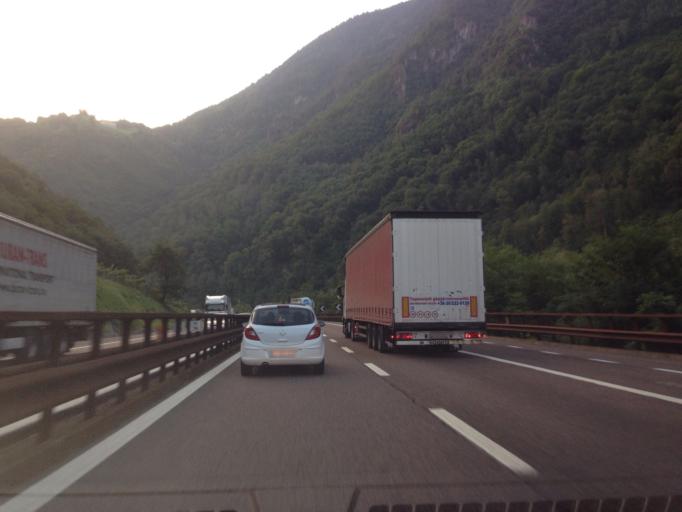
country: IT
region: Trentino-Alto Adige
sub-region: Bolzano
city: Cornedo All'Isarco
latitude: 46.4905
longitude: 11.4195
